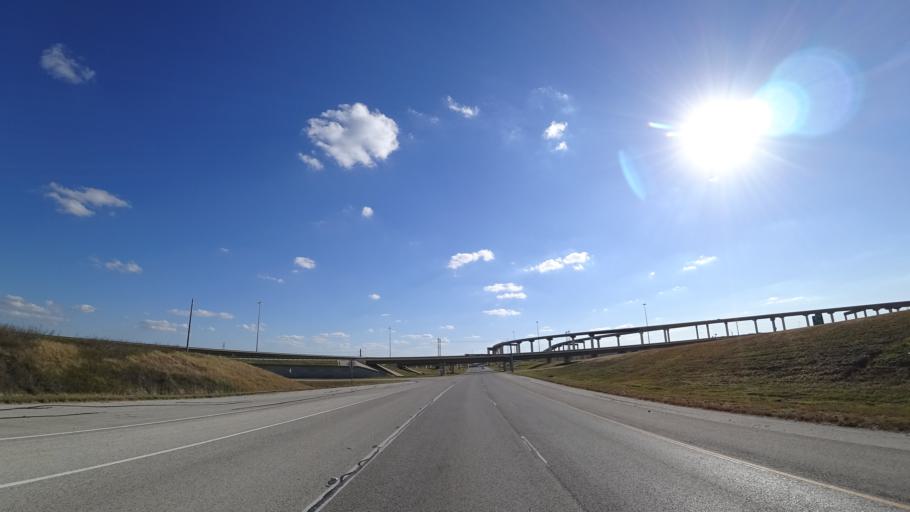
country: US
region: Texas
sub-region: Travis County
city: Onion Creek
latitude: 30.0837
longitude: -97.6919
